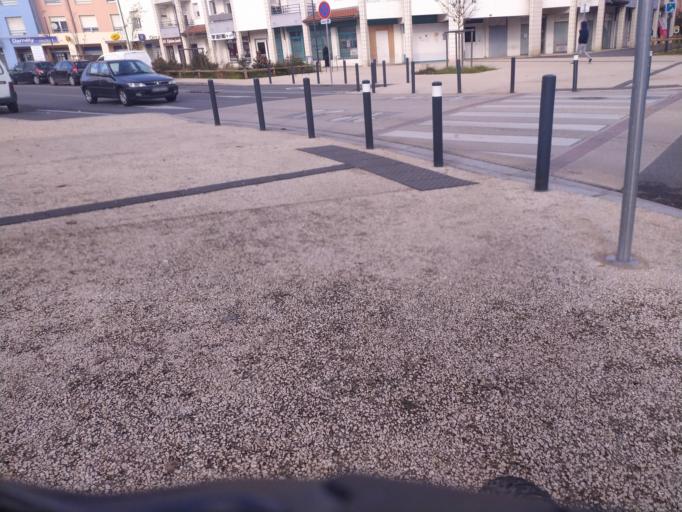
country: FR
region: Midi-Pyrenees
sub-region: Departement de la Haute-Garonne
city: Blagnac
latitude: 43.5816
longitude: 1.3886
